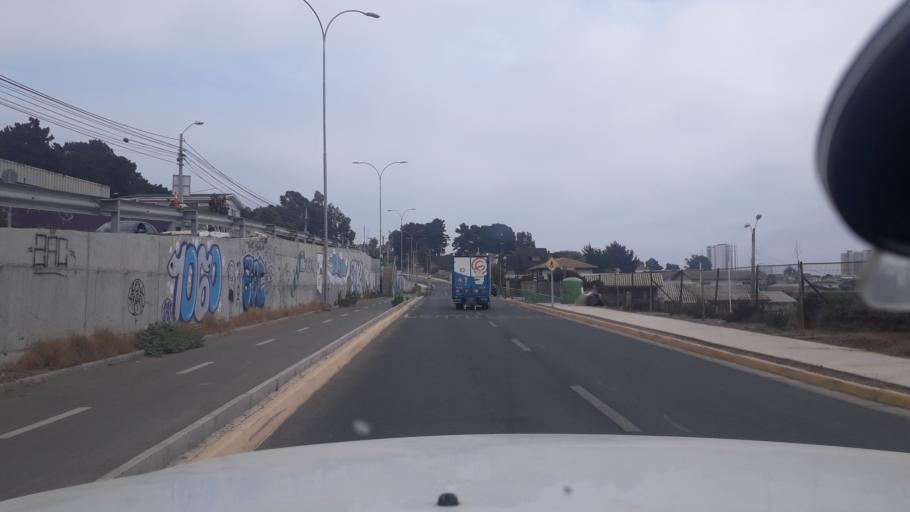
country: CL
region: Valparaiso
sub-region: Provincia de Valparaiso
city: Vina del Mar
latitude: -32.9374
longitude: -71.5345
